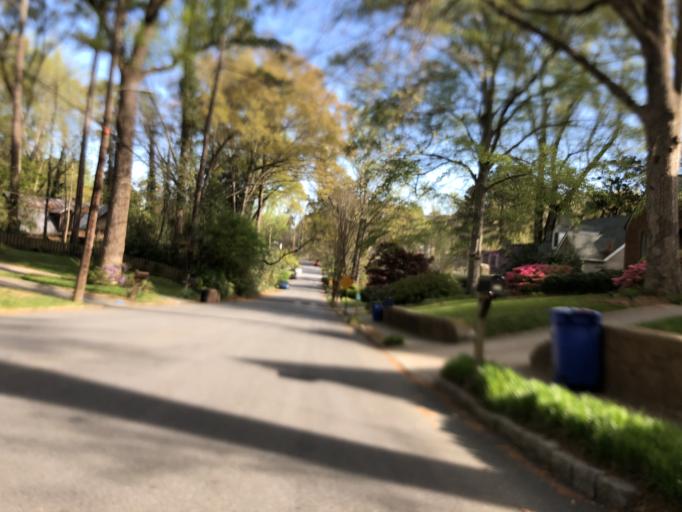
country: US
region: Georgia
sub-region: DeKalb County
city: North Decatur
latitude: 33.7888
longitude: -84.2997
